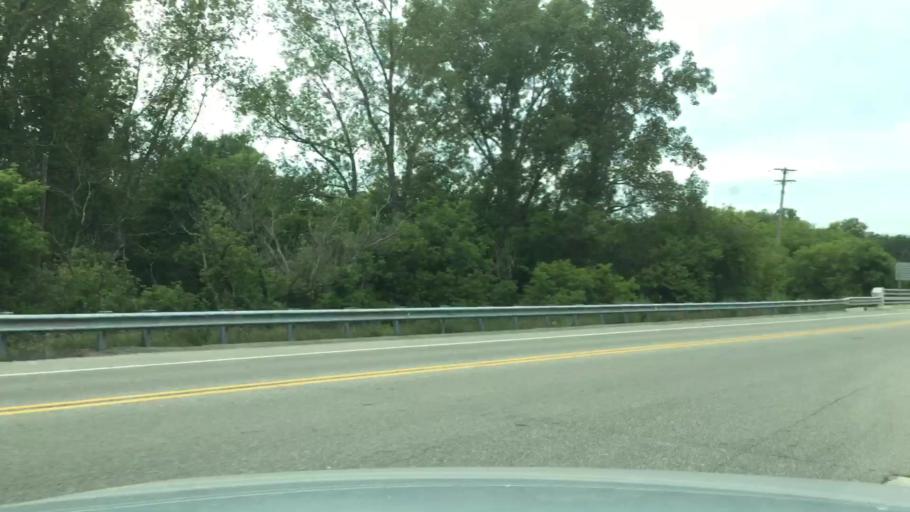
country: US
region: Michigan
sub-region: Shiawassee County
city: Durand
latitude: 42.9285
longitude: -84.0021
